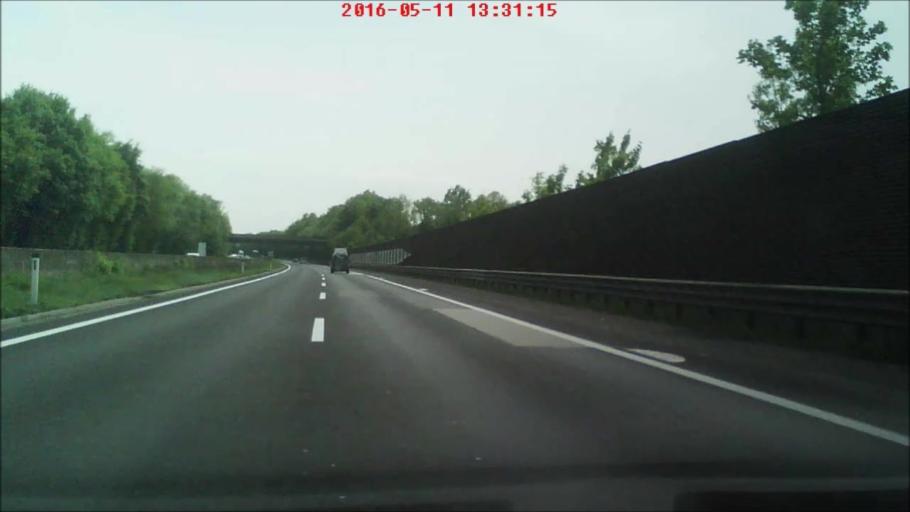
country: AT
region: Upper Austria
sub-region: Politischer Bezirk Scharding
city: Sankt Marienkirchen bei Schaerding
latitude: 48.3431
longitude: 13.4049
